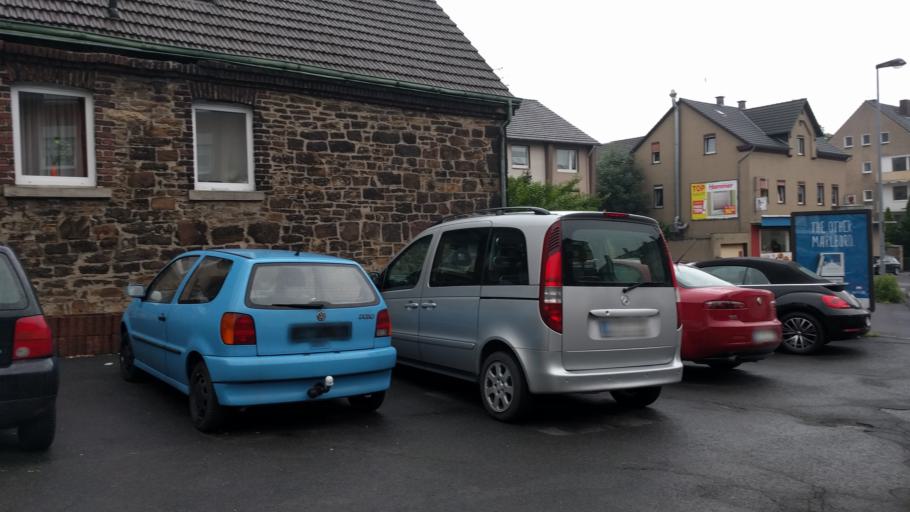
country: DE
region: North Rhine-Westphalia
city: Witten
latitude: 51.4534
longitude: 7.3755
